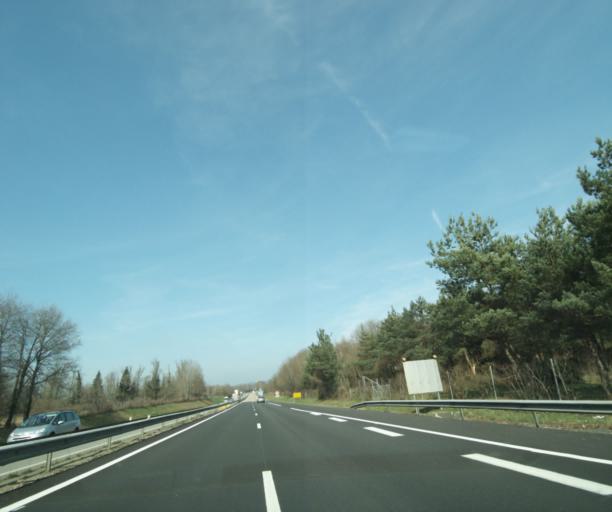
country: FR
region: Limousin
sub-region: Departement de la Haute-Vienne
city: Rilhac-Rancon
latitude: 45.8999
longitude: 1.2922
